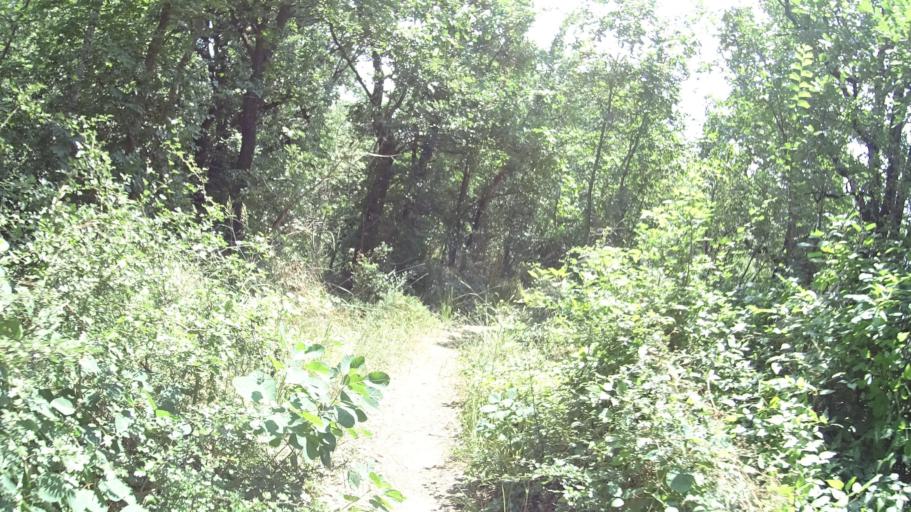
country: HU
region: Veszprem
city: Tihany
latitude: 46.8954
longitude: 17.8706
